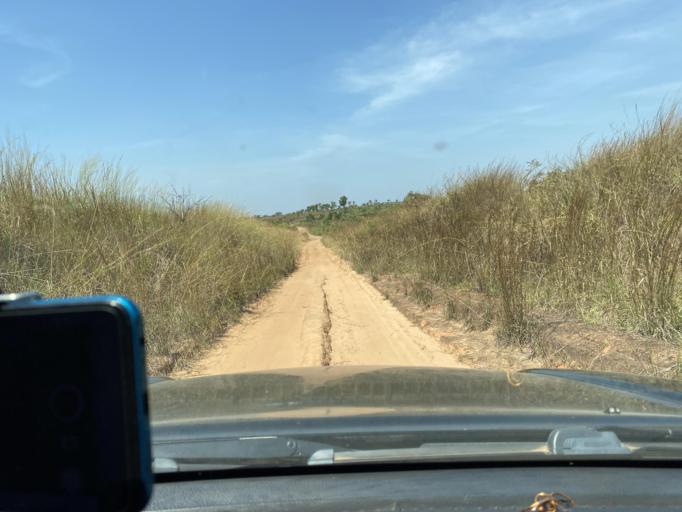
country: CD
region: Kasai-Oriental
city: Kabinda
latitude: -5.8782
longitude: 24.8654
